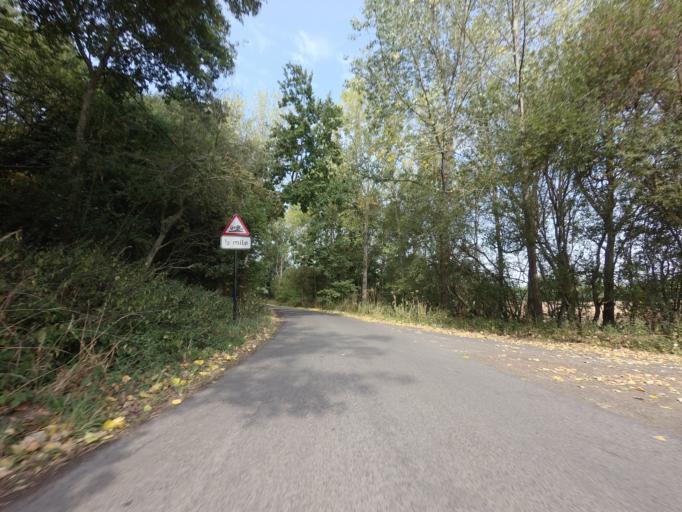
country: GB
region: England
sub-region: Kent
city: Headcorn
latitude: 51.1219
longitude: 0.5993
